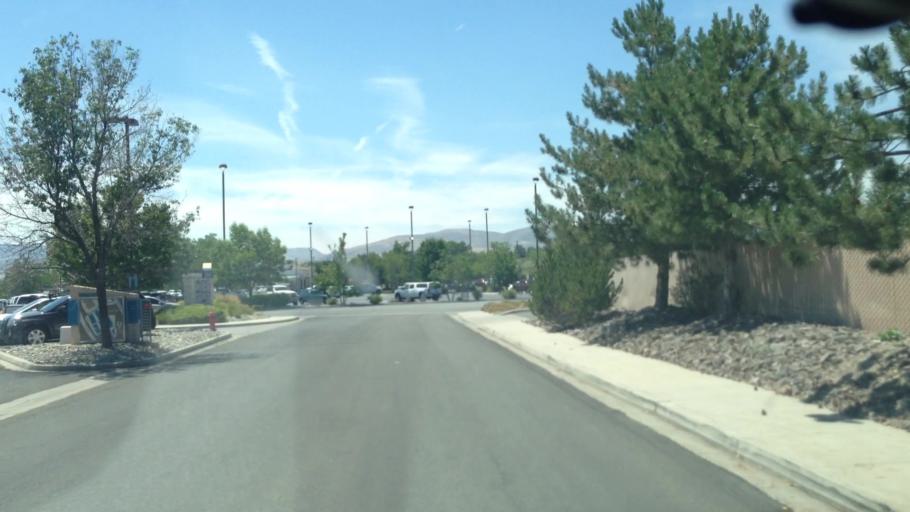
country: US
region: Nevada
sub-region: Washoe County
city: Sparks
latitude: 39.4428
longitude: -119.7699
